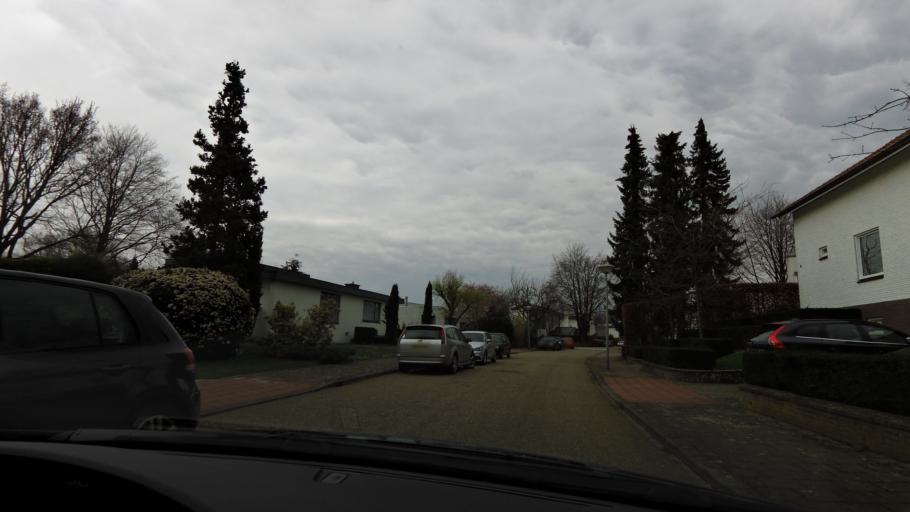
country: NL
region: Limburg
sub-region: Gemeente Sittard-Geleen
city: Sittard
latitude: 50.9916
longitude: 5.8729
